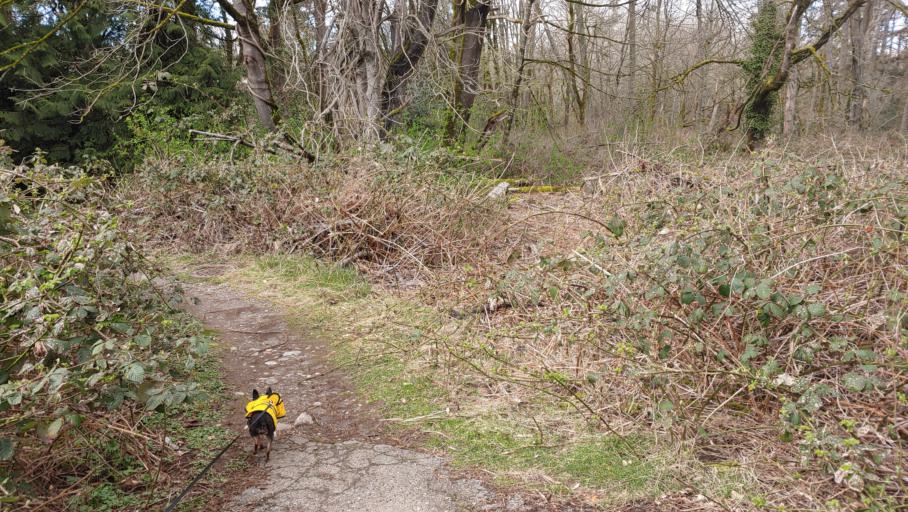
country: US
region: Washington
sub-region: King County
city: Des Moines
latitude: 47.4119
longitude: -122.3104
